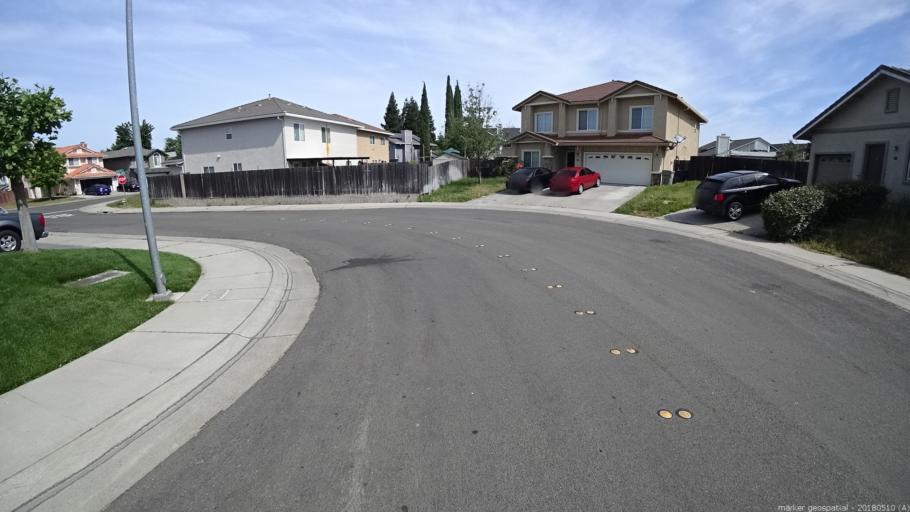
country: US
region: California
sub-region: Sacramento County
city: Rio Linda
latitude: 38.6563
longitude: -121.4581
